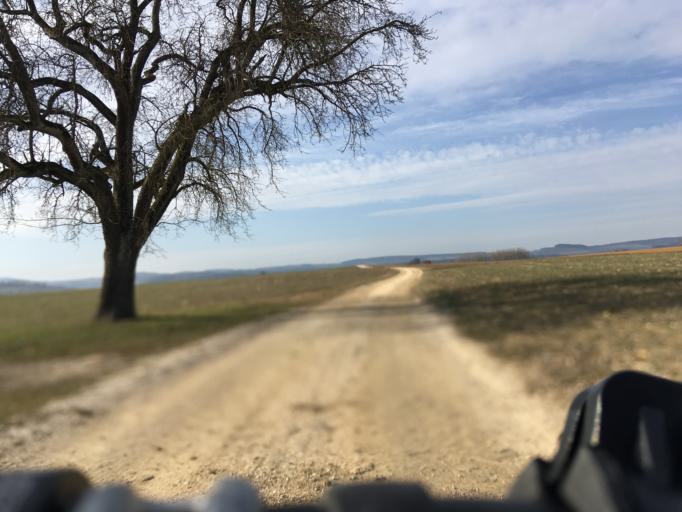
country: CH
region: Schaffhausen
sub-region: Bezirk Reiat
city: Thayngen
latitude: 47.7766
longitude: 8.7152
